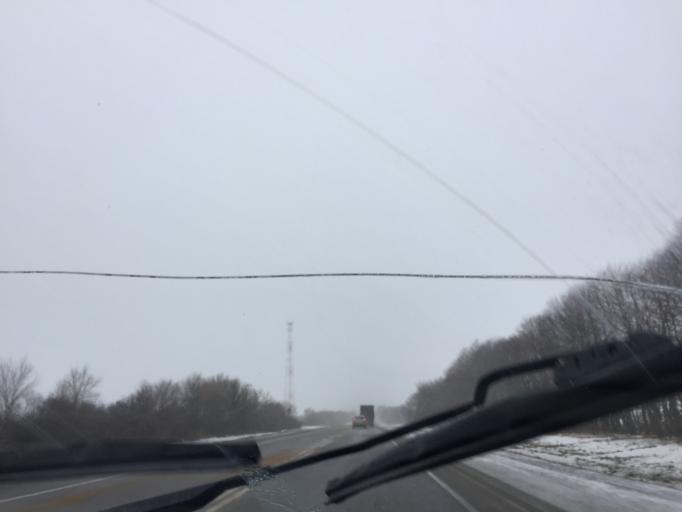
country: RU
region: Tula
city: Plavsk
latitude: 53.7873
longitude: 37.3658
